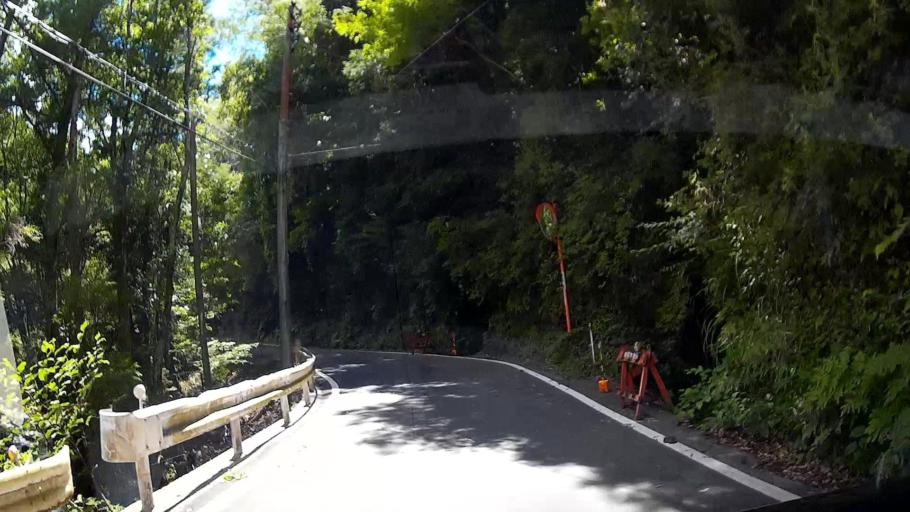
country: JP
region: Shizuoka
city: Shizuoka-shi
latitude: 35.1760
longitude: 138.3045
